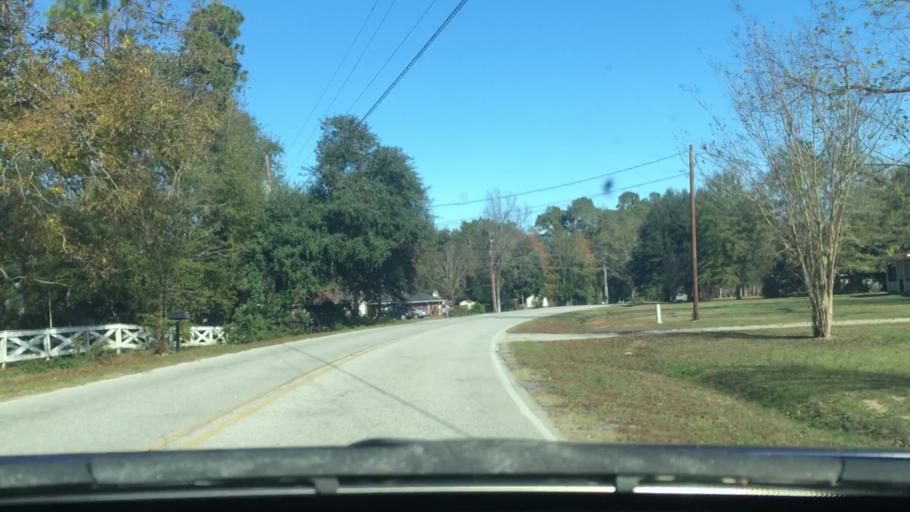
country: US
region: South Carolina
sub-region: Sumter County
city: Cane Savannah
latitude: 33.9125
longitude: -80.4119
